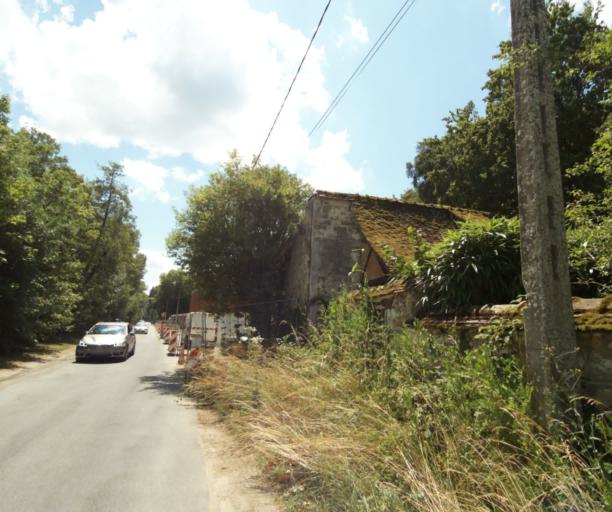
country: FR
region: Ile-de-France
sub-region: Departement de Seine-et-Marne
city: Samoreau
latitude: 48.4350
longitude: 2.7443
